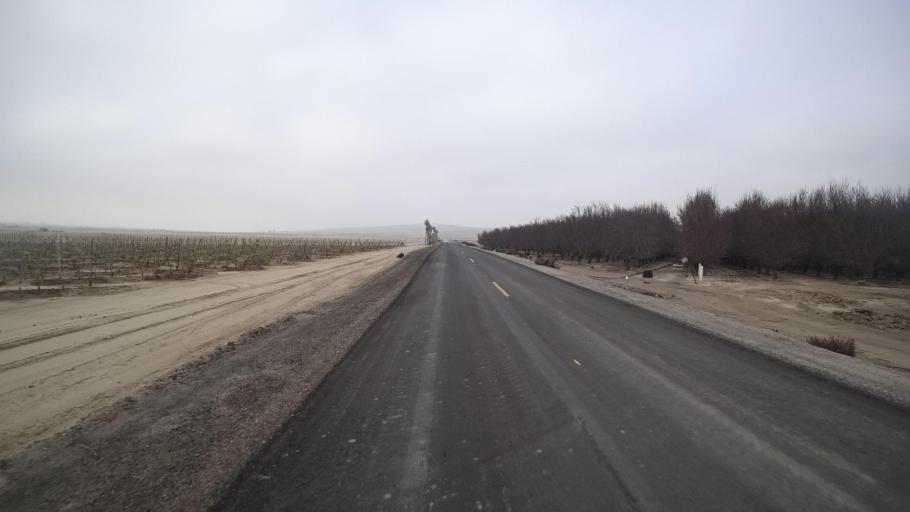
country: US
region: California
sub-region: Kern County
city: Maricopa
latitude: 35.1192
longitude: -119.3576
